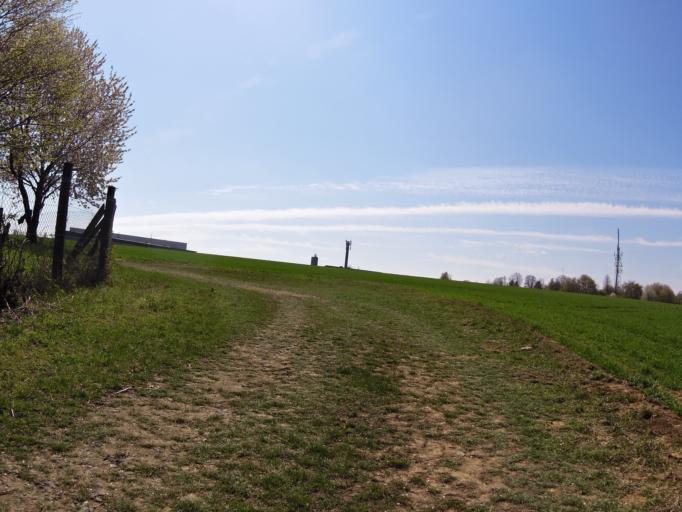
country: DE
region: Bavaria
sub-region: Regierungsbezirk Unterfranken
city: Biebelried
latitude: 49.7855
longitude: 10.0681
